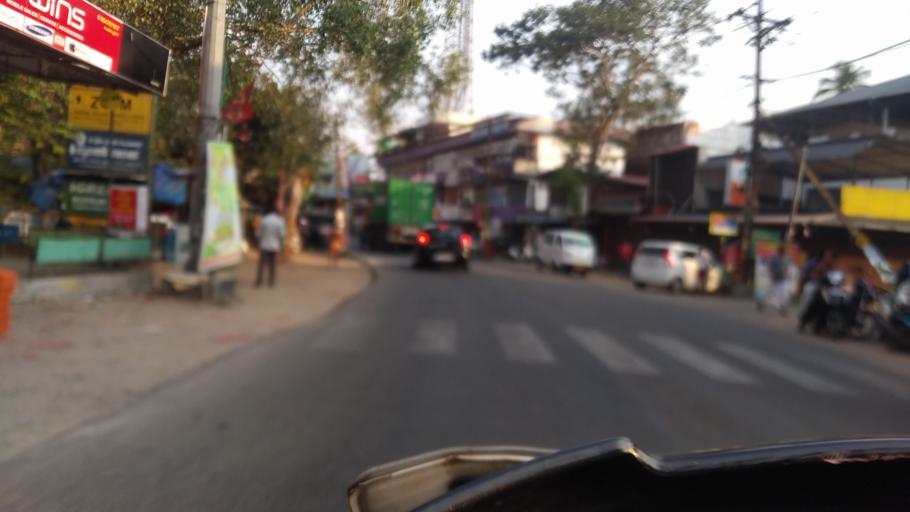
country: IN
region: Kerala
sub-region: Thrissur District
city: Thanniyam
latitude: 10.3556
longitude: 76.1282
